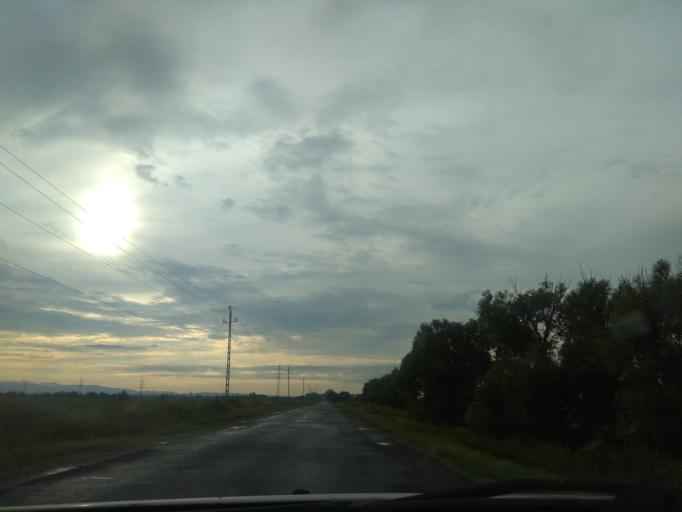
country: HU
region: Borsod-Abauj-Zemplen
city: Onga
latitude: 48.1144
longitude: 20.9426
